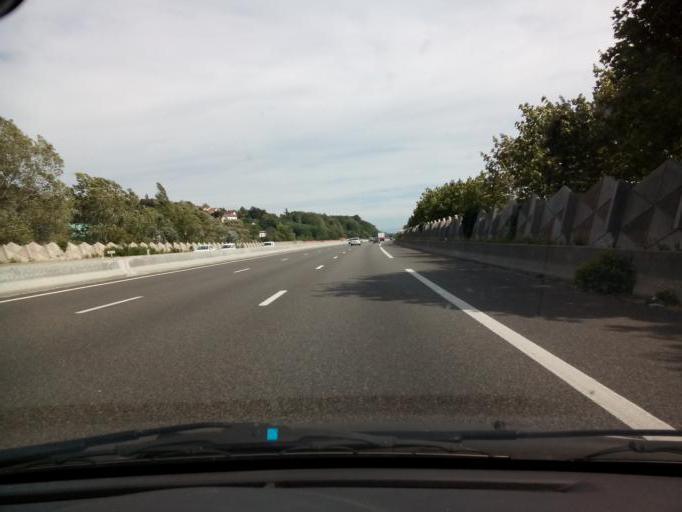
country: FR
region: Rhone-Alpes
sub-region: Departement de l'Isere
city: Bourgoin-Jallieu
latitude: 45.6002
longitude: 5.2702
